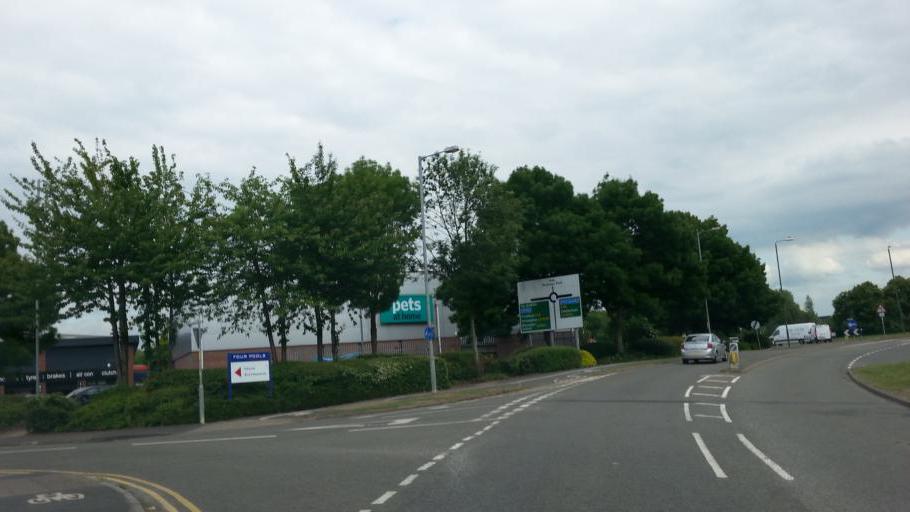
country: GB
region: England
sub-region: Worcestershire
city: Evesham
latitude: 52.0777
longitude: -1.9381
